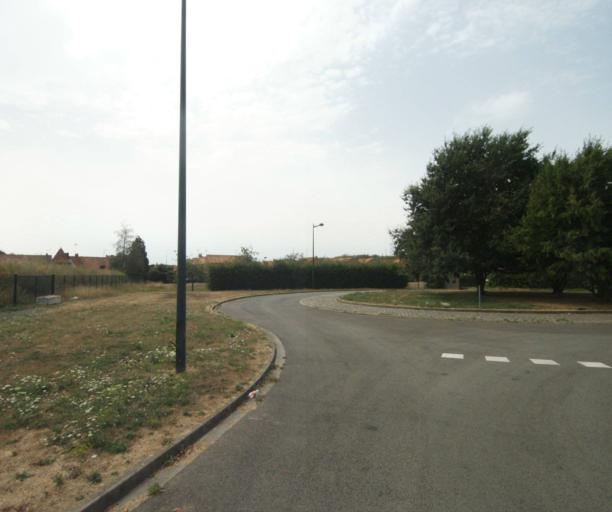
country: FR
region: Nord-Pas-de-Calais
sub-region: Departement du Nord
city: Wattrelos
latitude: 50.6921
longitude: 3.2298
